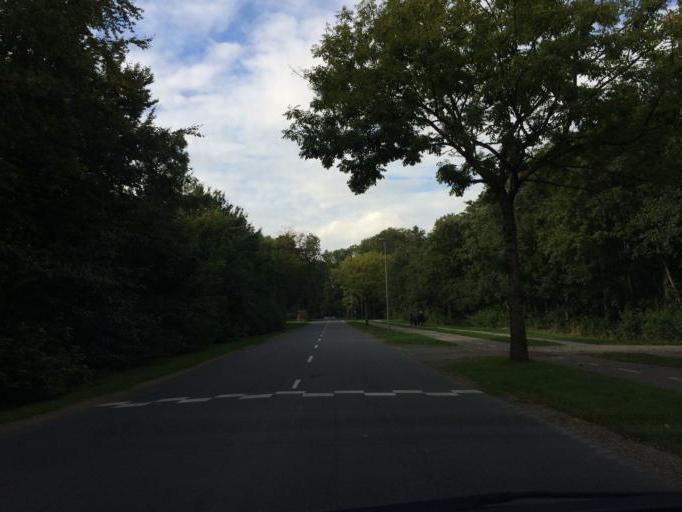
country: DK
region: North Denmark
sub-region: Bronderslev Kommune
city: Dronninglund
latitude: 57.1537
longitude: 10.2768
